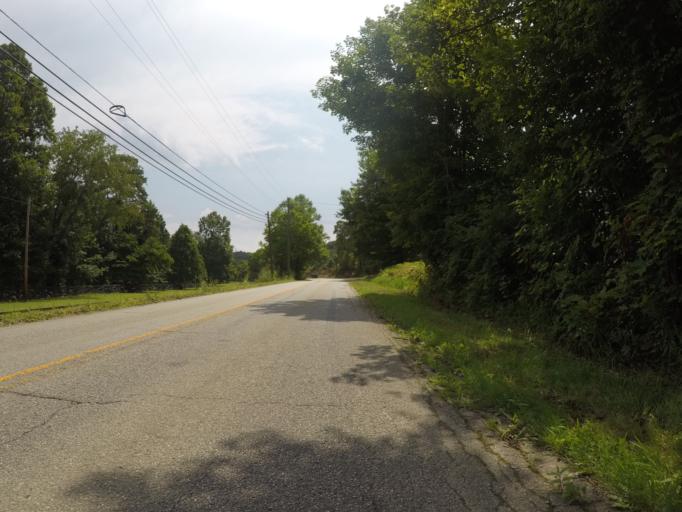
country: US
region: Kentucky
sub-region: Boyd County
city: Ironville
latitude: 38.4456
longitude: -82.6944
